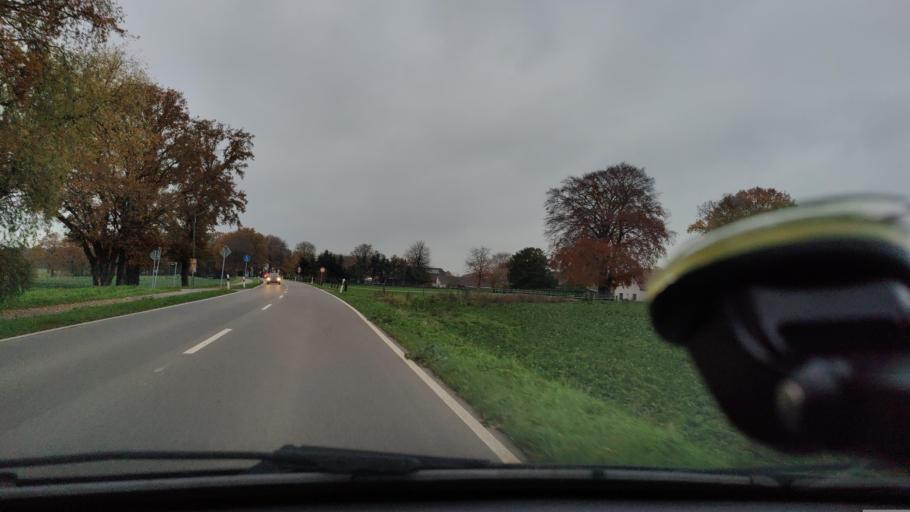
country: DE
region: North Rhine-Westphalia
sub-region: Regierungsbezirk Dusseldorf
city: Alpen
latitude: 51.5988
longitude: 6.5024
